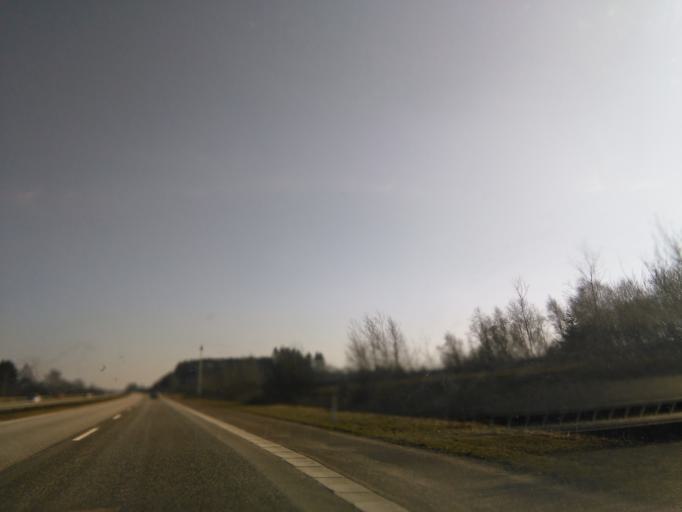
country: DK
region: South Denmark
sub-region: Assens Kommune
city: Vissenbjerg
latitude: 55.4006
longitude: 10.1582
